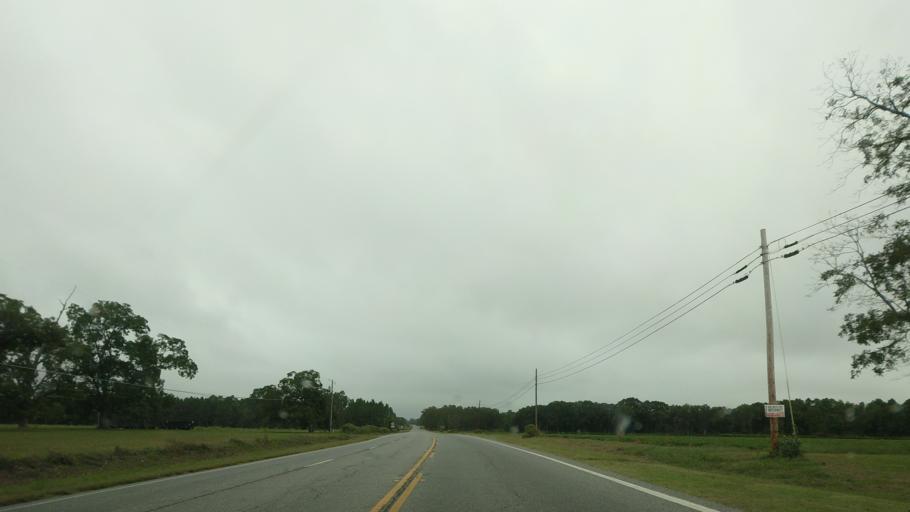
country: US
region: Georgia
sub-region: Ben Hill County
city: Fitzgerald
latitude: 31.6666
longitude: -83.2348
